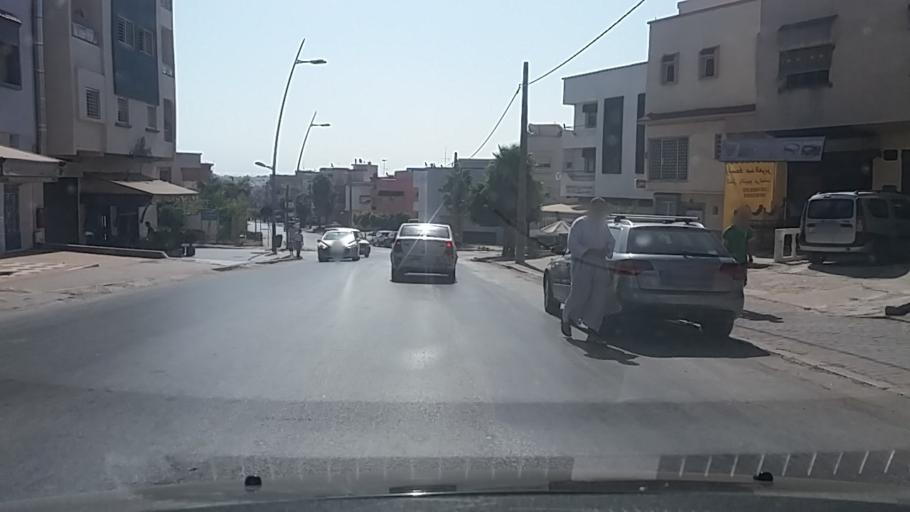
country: MA
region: Gharb-Chrarda-Beni Hssen
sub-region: Kenitra Province
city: Kenitra
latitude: 34.2658
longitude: -6.6142
